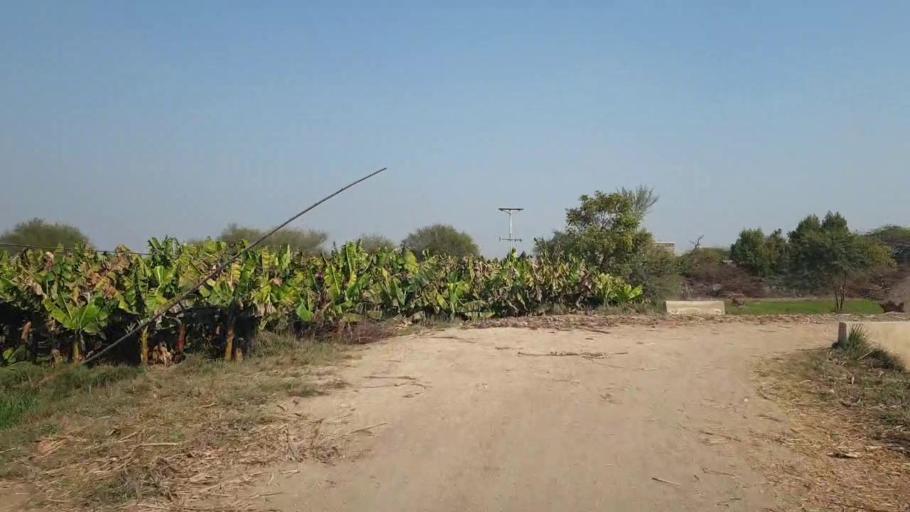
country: PK
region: Sindh
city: Mirwah Gorchani
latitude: 25.3882
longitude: 68.9561
